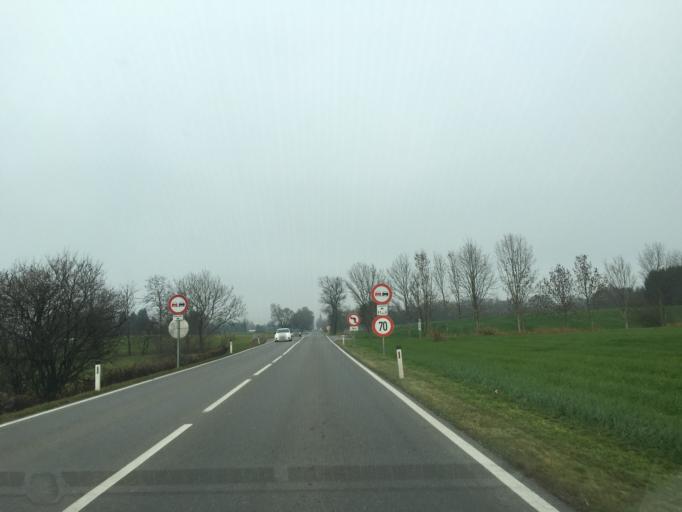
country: CH
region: Saint Gallen
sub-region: Wahlkreis Rheintal
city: Diepoldsau
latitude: 47.4050
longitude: 9.6730
